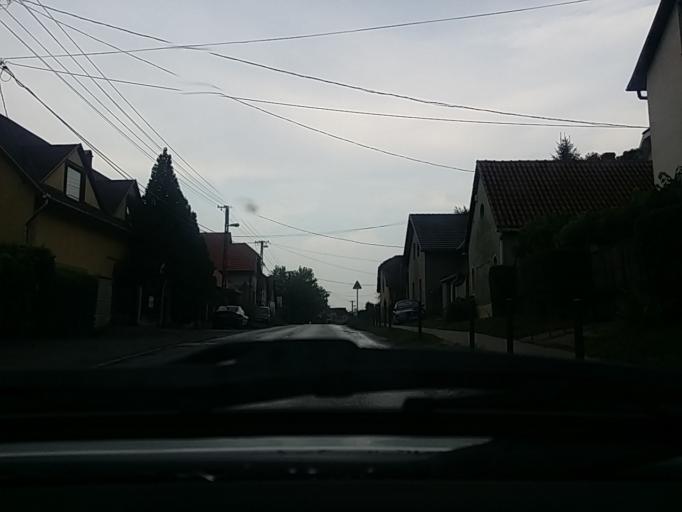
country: HU
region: Pest
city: Budakeszi
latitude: 47.5064
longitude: 18.9199
